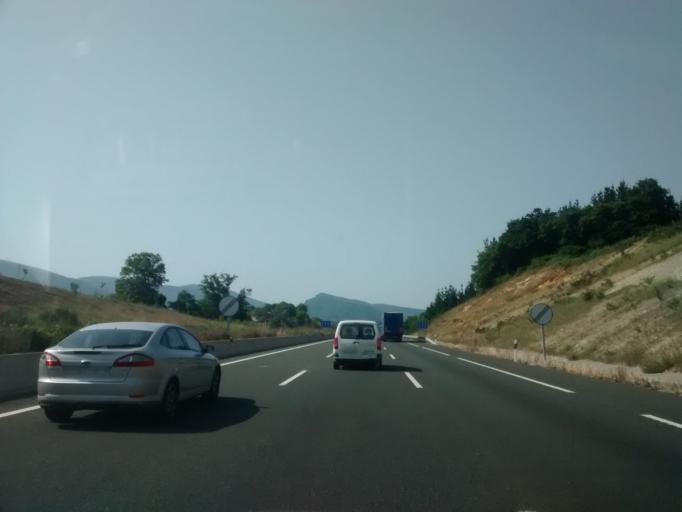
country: ES
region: Cantabria
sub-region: Provincia de Cantabria
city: Molledo
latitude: 43.1510
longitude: -4.0540
